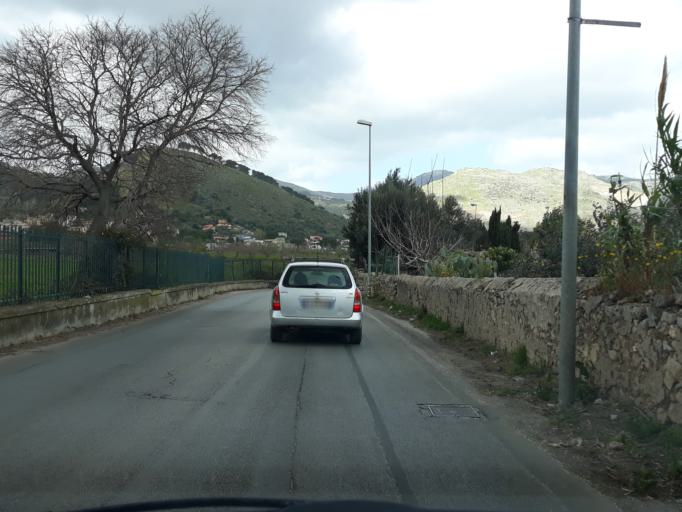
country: IT
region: Sicily
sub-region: Palermo
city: Piano dei Geli
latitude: 38.1142
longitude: 13.3043
